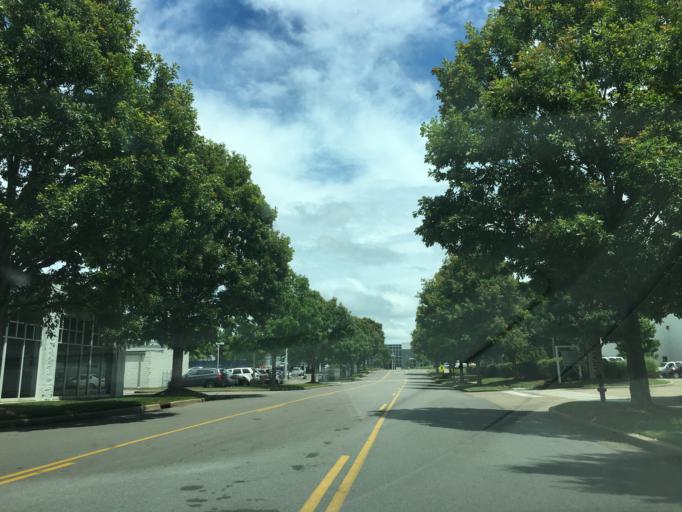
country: US
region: Tennessee
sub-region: Davidson County
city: Oak Hill
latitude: 36.1042
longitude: -86.7613
